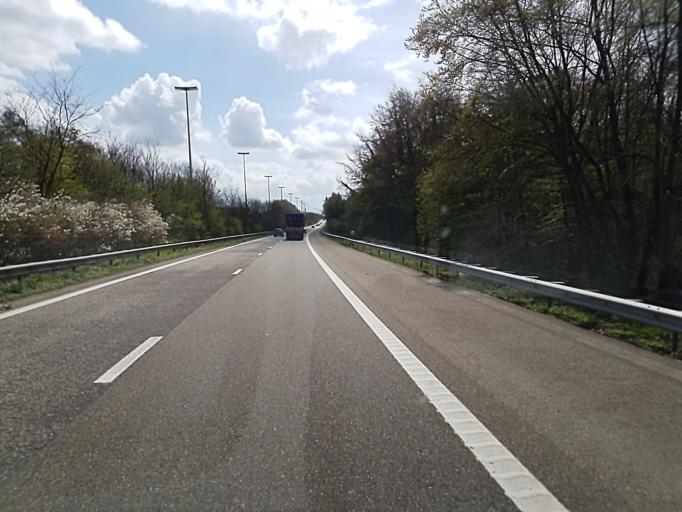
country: BE
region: Flanders
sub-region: Provincie Limburg
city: Hoeselt
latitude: 50.8521
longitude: 5.5036
